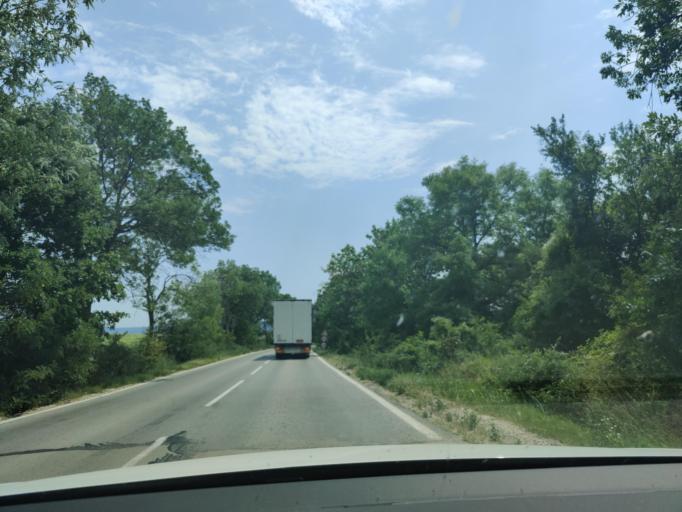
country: BG
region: Vidin
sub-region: Obshtina Ruzhintsi
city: Ruzhintsi
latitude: 43.6345
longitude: 22.8171
